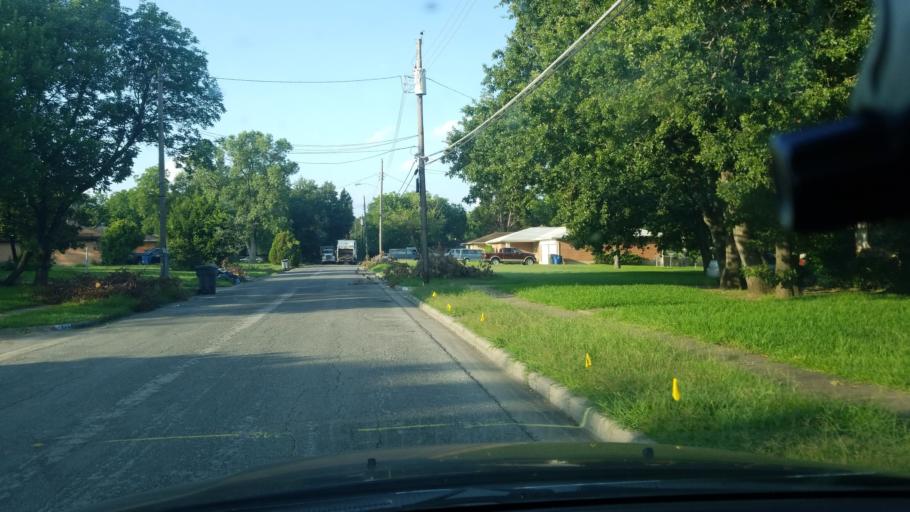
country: US
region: Texas
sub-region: Dallas County
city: Balch Springs
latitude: 32.7162
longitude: -96.6915
